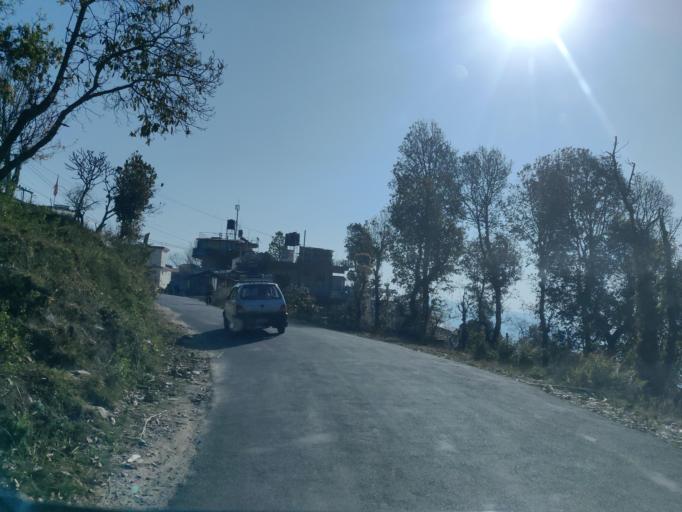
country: NP
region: Western Region
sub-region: Gandaki Zone
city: Pokhara
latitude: 28.2441
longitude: 83.9556
